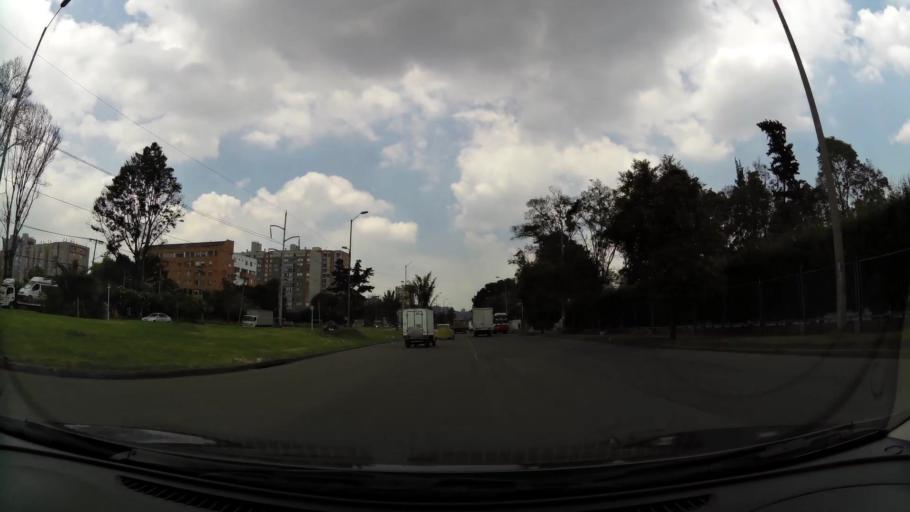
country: CO
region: Cundinamarca
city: Cota
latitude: 4.7531
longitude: -74.0522
